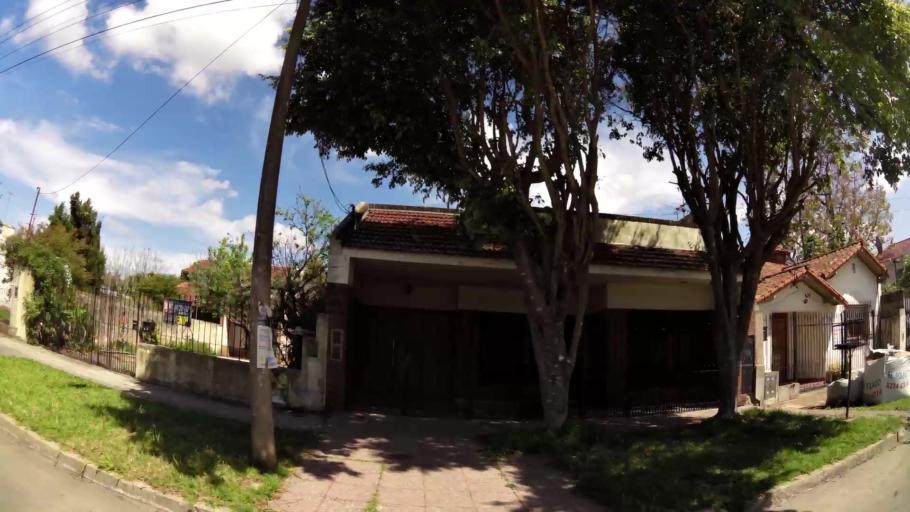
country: AR
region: Buenos Aires
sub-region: Partido de Quilmes
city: Quilmes
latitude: -34.8150
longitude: -58.2737
